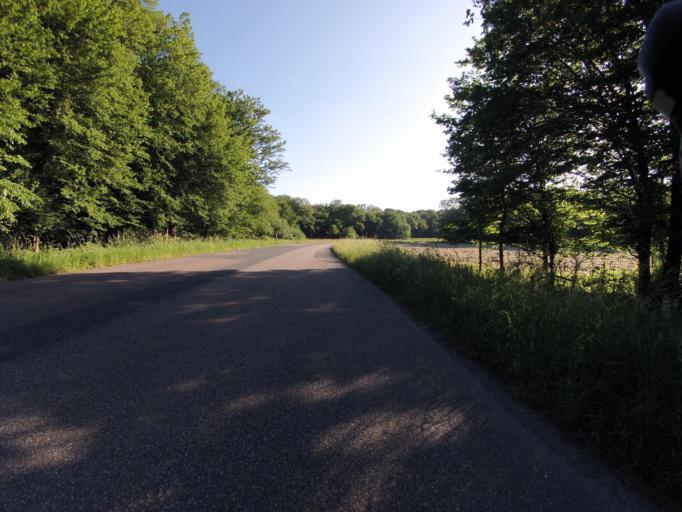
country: DE
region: Lower Saxony
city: Bad Bentheim
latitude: 52.3118
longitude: 7.1522
